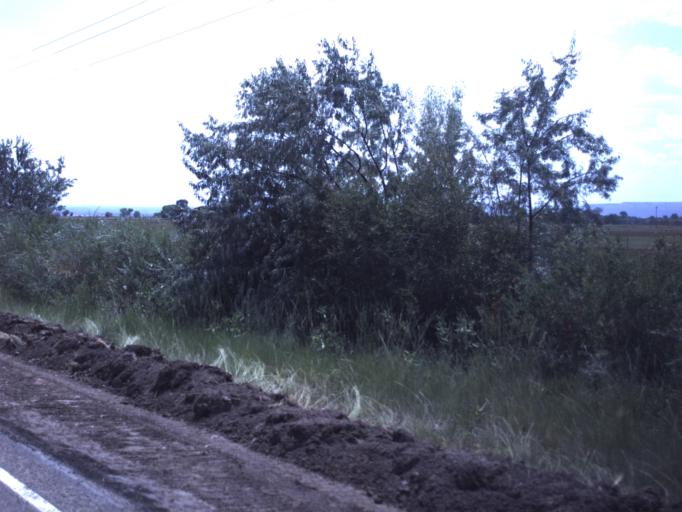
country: US
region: Utah
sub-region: Duchesne County
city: Roosevelt
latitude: 40.4173
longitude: -110.0300
